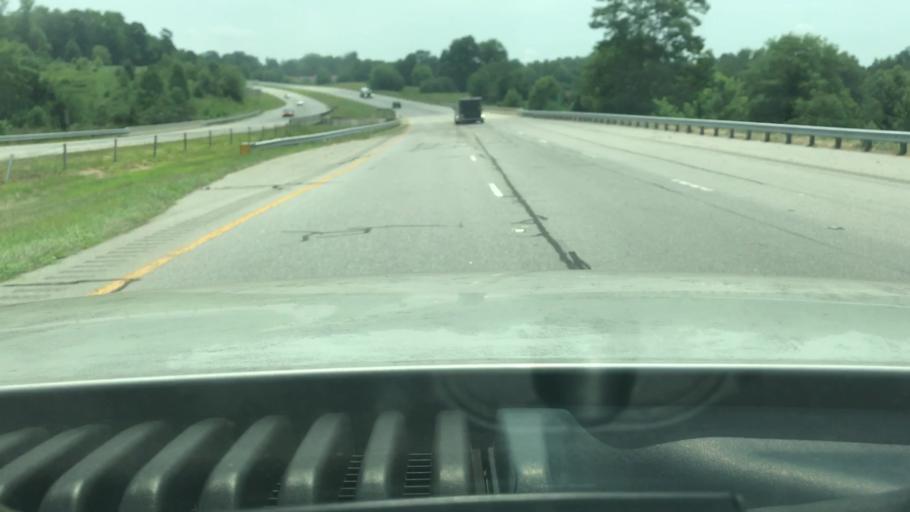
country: US
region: North Carolina
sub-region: Yadkin County
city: Jonesville
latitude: 36.1430
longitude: -80.8956
